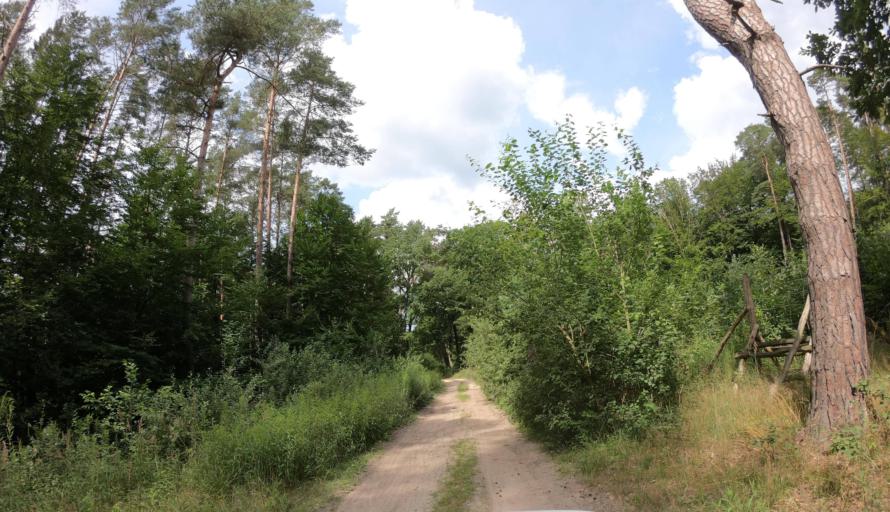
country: PL
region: West Pomeranian Voivodeship
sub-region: Powiat gryfinski
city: Stare Czarnowo
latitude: 53.3337
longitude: 14.8054
